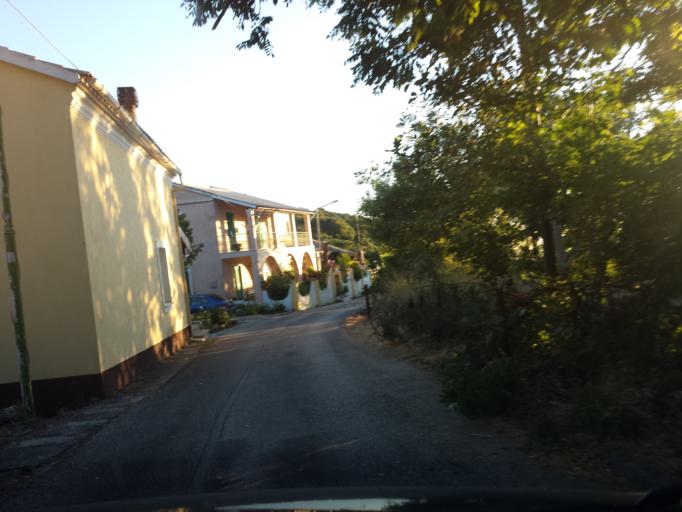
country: GR
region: Ionian Islands
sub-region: Nomos Kerkyras
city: Acharavi
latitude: 39.7436
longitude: 19.8370
